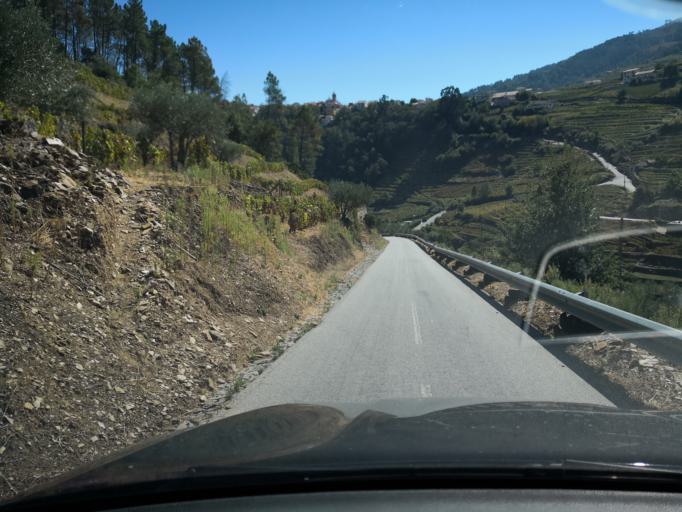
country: PT
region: Vila Real
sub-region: Santa Marta de Penaguiao
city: Santa Marta de Penaguiao
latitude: 41.2518
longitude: -7.8144
